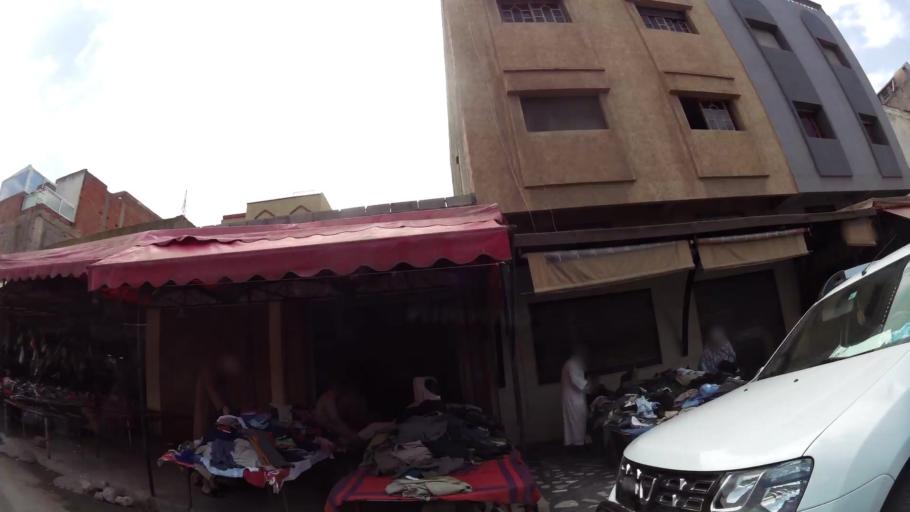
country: MA
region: Rabat-Sale-Zemmour-Zaer
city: Sale
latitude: 34.0547
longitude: -6.8195
